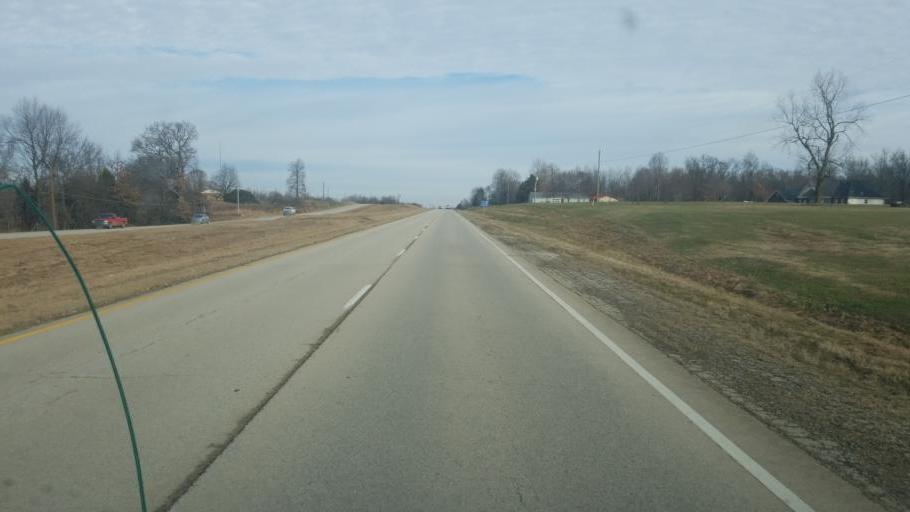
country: US
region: Missouri
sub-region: Stoddard County
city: Bloomfield
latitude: 36.8471
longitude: -89.9405
